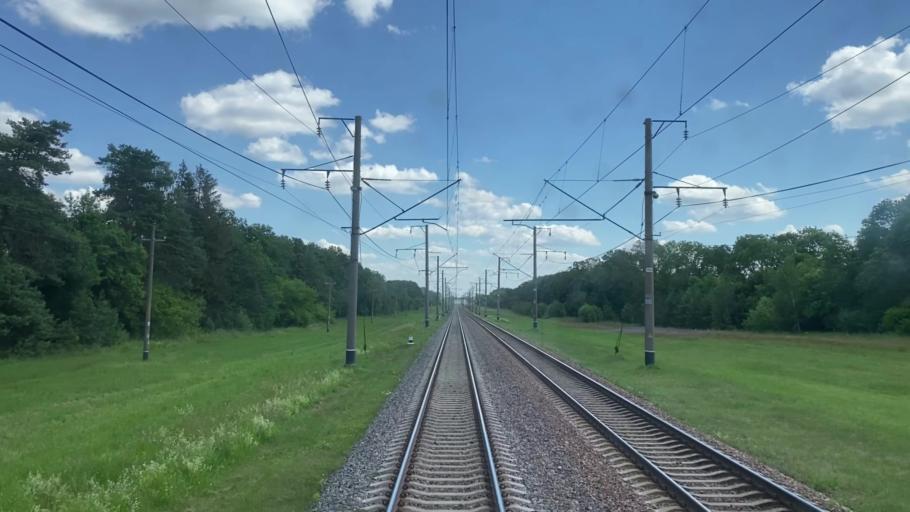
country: BY
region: Brest
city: Ivatsevichy
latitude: 52.8348
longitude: 25.5039
